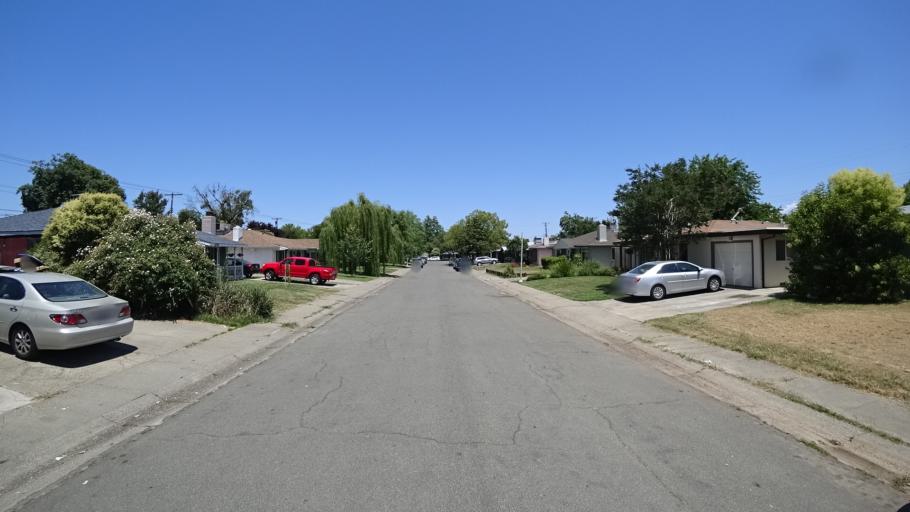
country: US
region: California
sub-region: Sacramento County
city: Parkway
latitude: 38.5274
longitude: -121.4379
